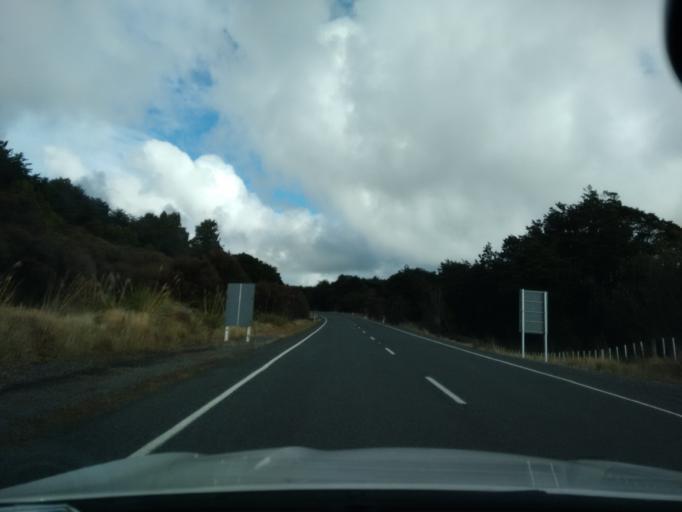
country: NZ
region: Manawatu-Wanganui
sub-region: Ruapehu District
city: Waiouru
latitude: -39.2988
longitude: 175.3882
